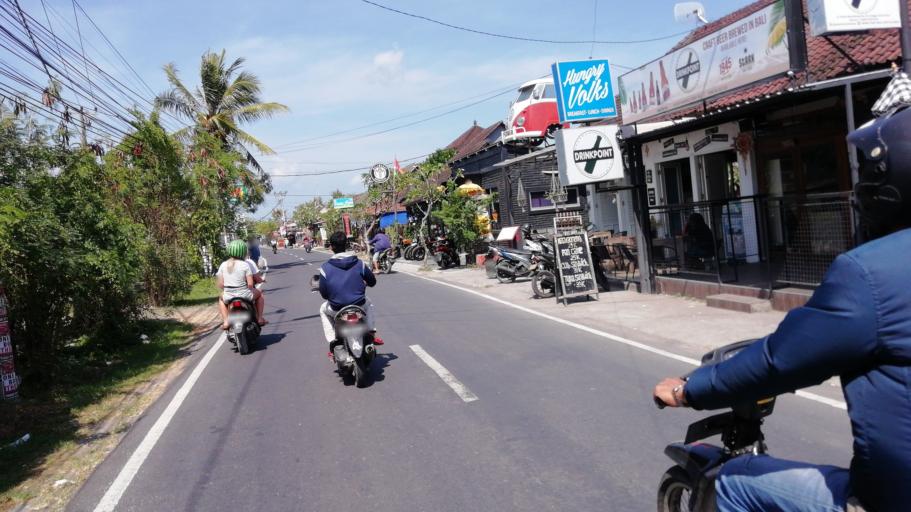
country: ID
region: Bali
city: Banjar Gunungpande
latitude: -8.6444
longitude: 115.1417
